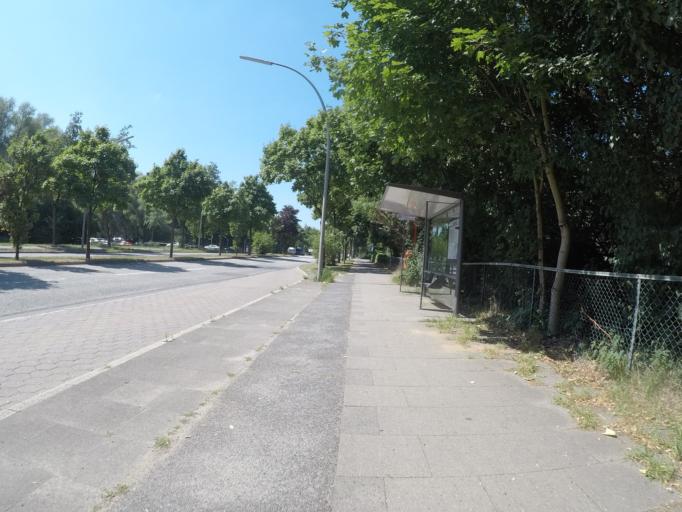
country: DE
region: Hamburg
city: Harburg
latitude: 53.4860
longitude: 10.0162
